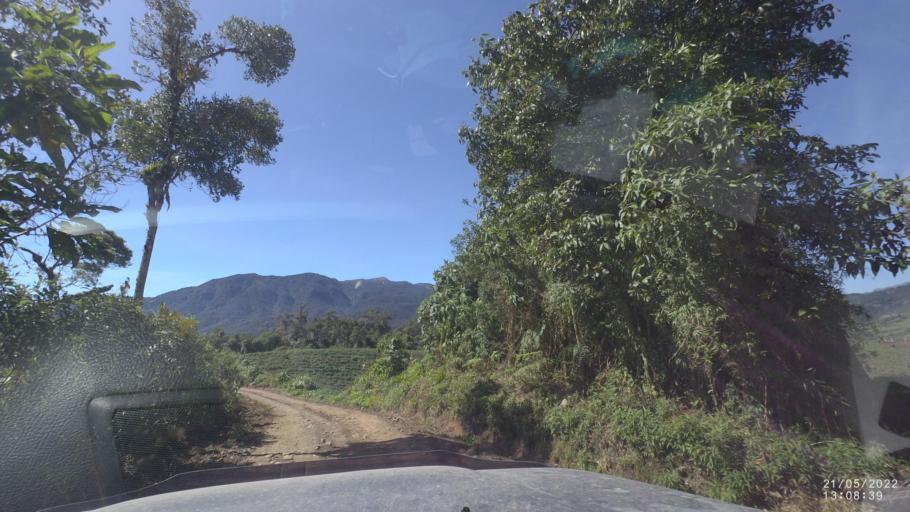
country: BO
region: Cochabamba
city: Colomi
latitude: -17.1471
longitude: -65.9422
